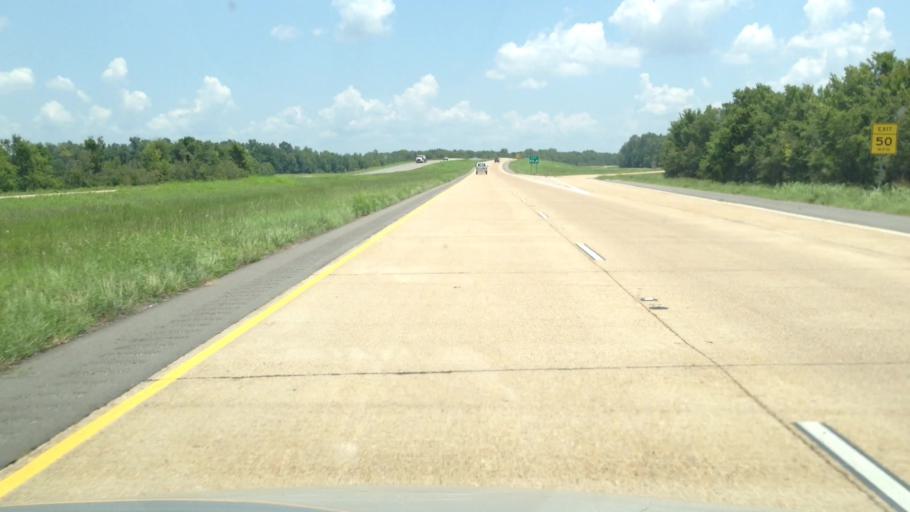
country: US
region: Louisiana
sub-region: Avoyelles Parish
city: Bunkie
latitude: 30.9897
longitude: -92.3135
